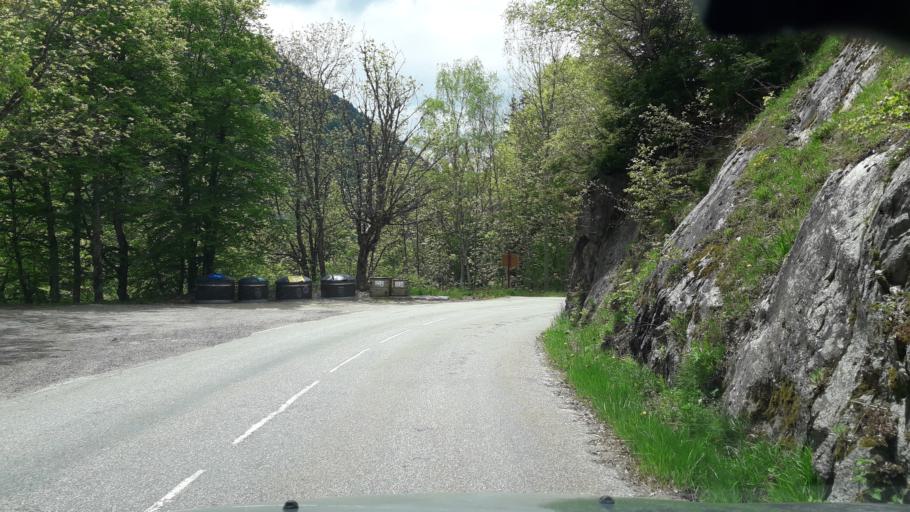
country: FR
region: Rhone-Alpes
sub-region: Departement de l'Isere
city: Theys
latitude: 45.1989
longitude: 6.0393
